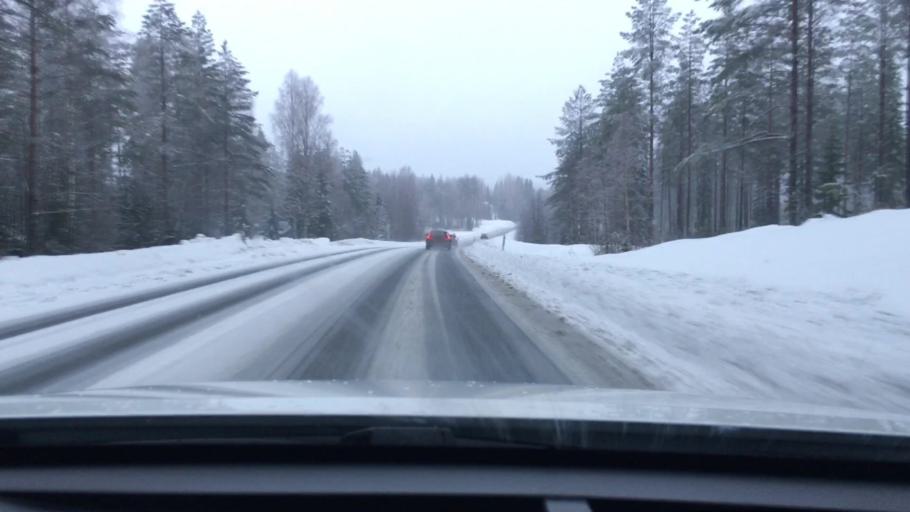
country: FI
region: Northern Savo
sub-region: Ylae-Savo
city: Sonkajaervi
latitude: 63.7648
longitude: 27.4106
